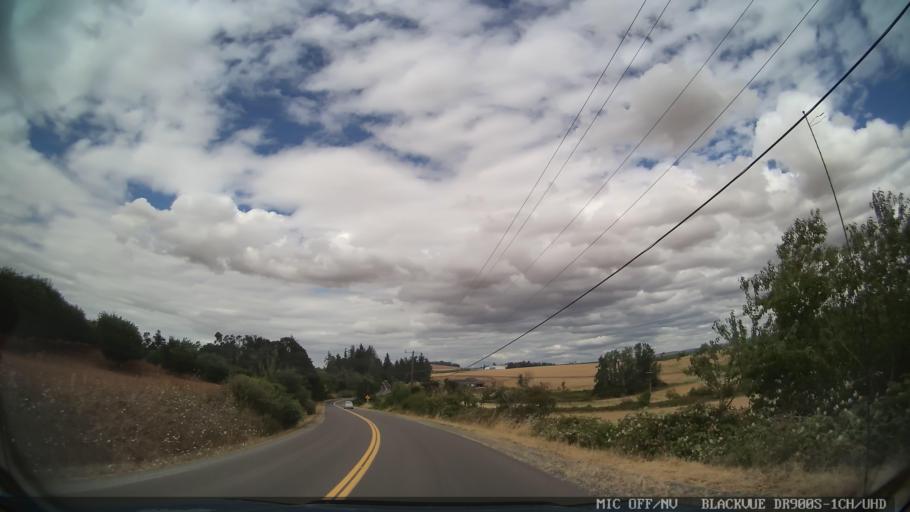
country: US
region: Oregon
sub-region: Marion County
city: Aumsville
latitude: 44.8607
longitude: -122.8518
